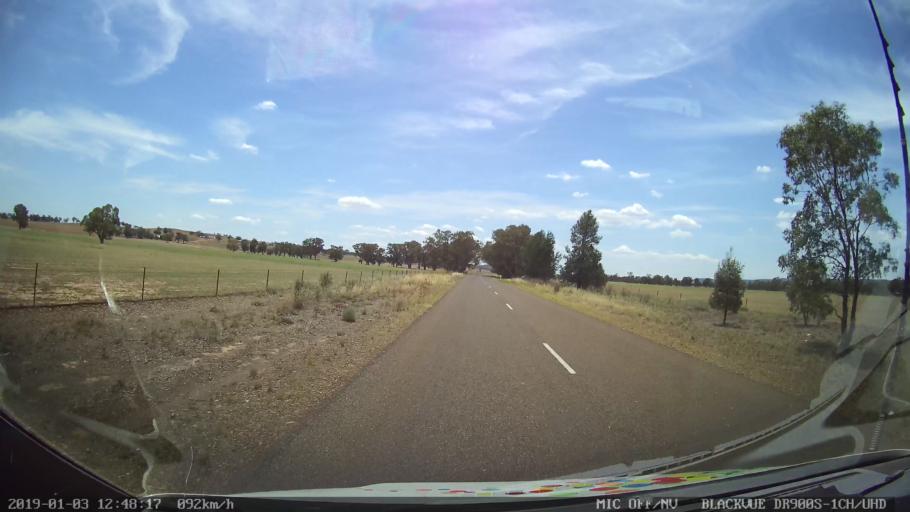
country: AU
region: New South Wales
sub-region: Weddin
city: Grenfell
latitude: -33.7163
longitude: 148.2492
